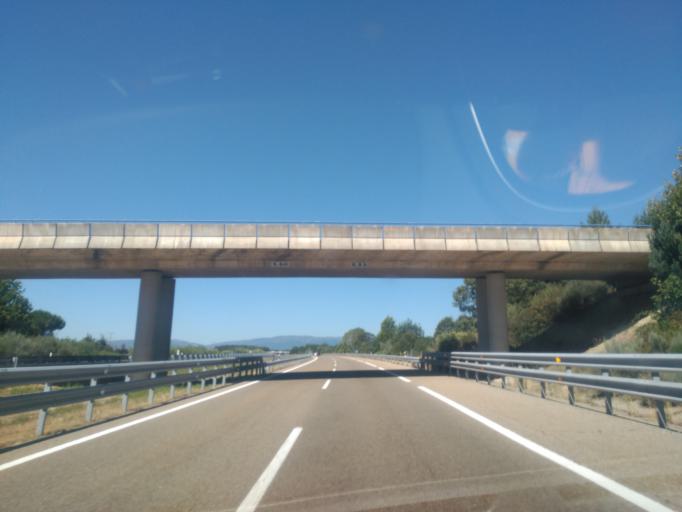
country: ES
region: Castille and Leon
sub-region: Provincia de Zamora
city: Asturianos
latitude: 42.0428
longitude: -6.4702
